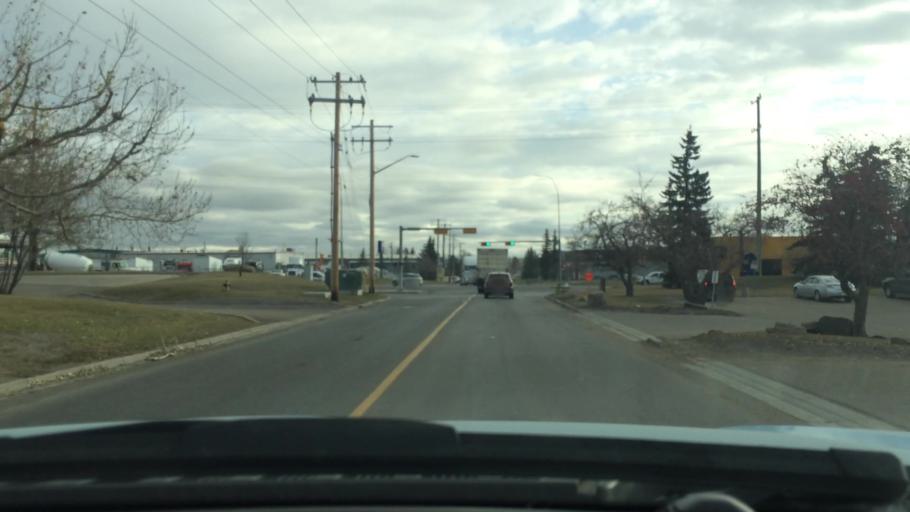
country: CA
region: Alberta
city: Calgary
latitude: 51.0037
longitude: -113.9600
